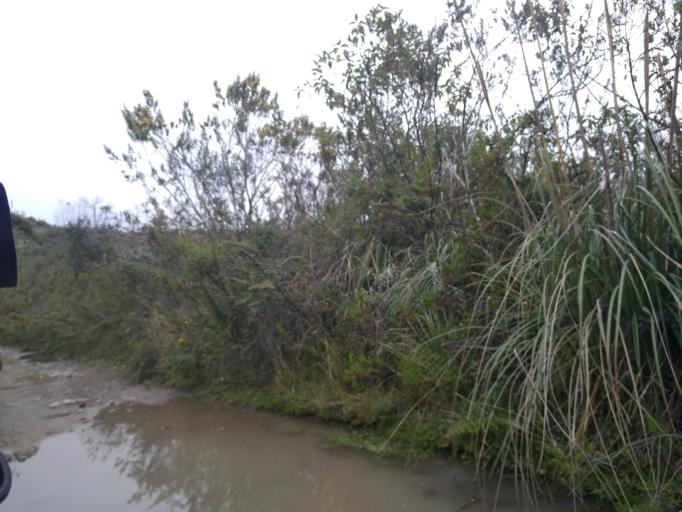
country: EC
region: Carchi
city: San Gabriel
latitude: 0.6981
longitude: -77.8441
